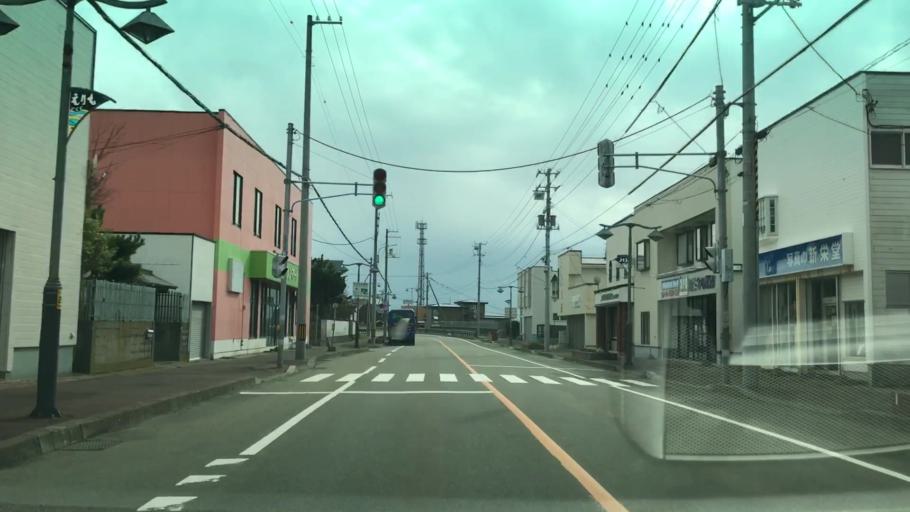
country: JP
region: Hokkaido
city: Shizunai-furukawacho
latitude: 42.0137
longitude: 143.1483
